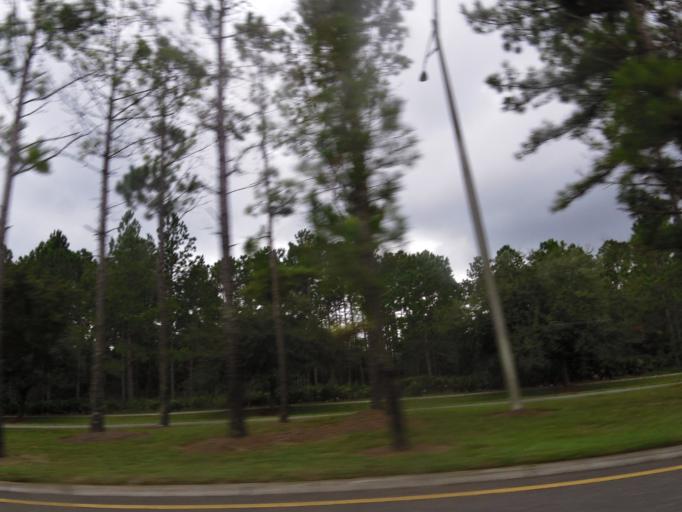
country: US
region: Florida
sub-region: Clay County
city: Bellair-Meadowbrook Terrace
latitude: 30.1949
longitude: -81.8192
